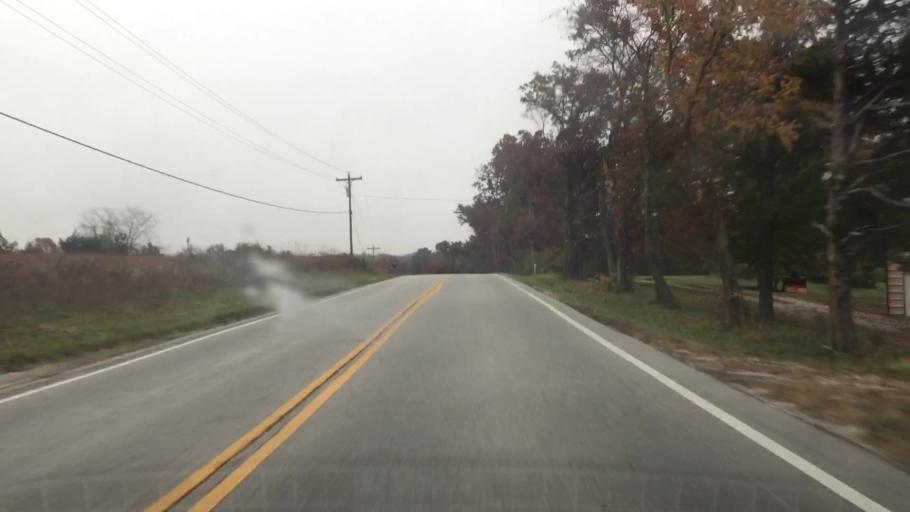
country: US
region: Missouri
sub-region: Callaway County
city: Fulton
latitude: 38.8847
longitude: -92.0946
